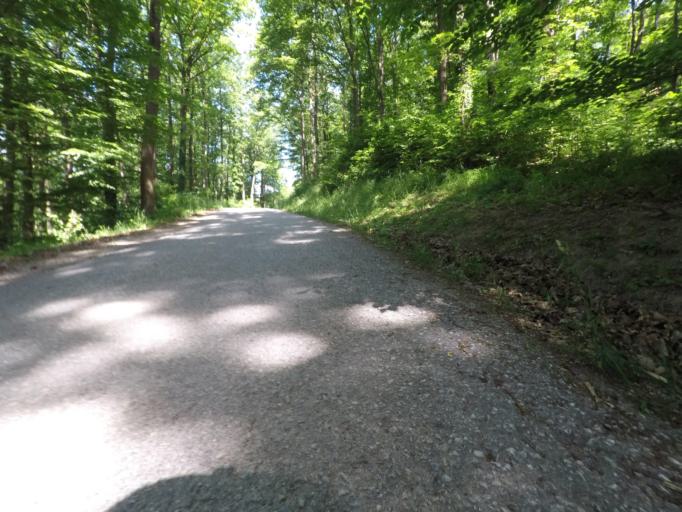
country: AT
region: Lower Austria
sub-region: Politischer Bezirk Modling
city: Perchtoldsdorf
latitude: 48.1738
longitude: 16.2428
